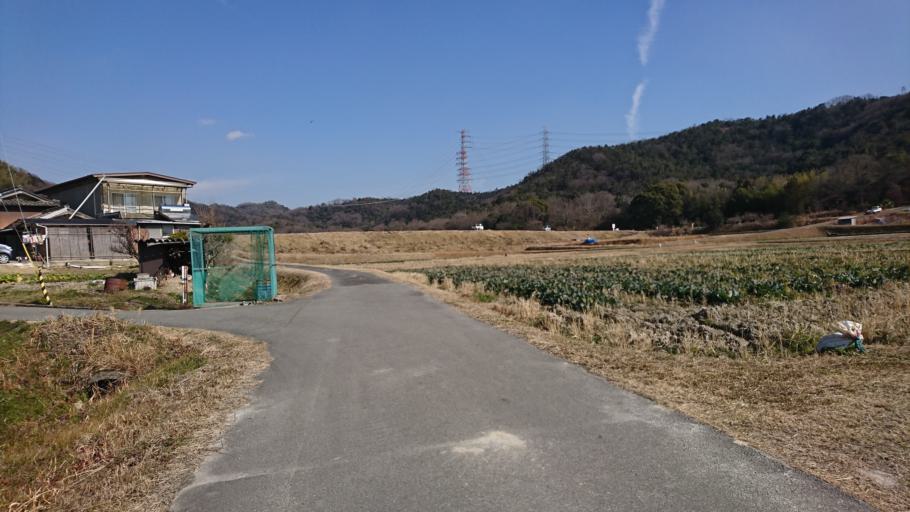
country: JP
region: Hyogo
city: Kakogawacho-honmachi
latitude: 34.8191
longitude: 134.8547
